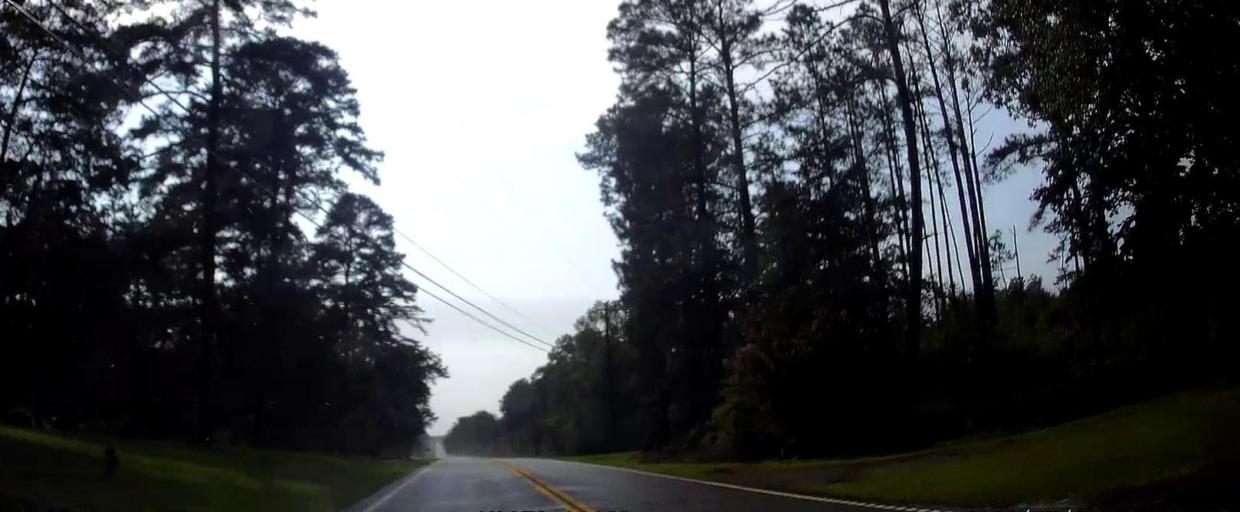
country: US
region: Georgia
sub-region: Twiggs County
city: Jeffersonville
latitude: 32.6040
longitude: -83.2507
